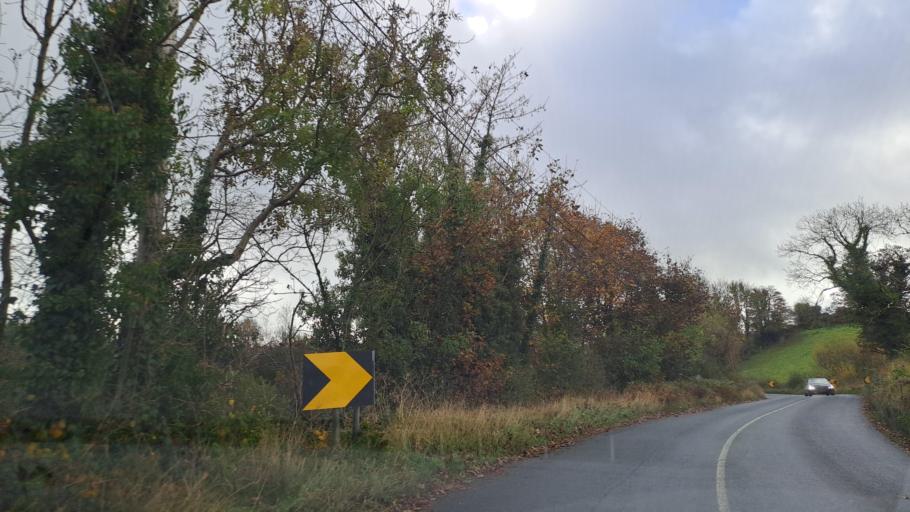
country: IE
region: Ulster
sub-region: An Cabhan
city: Virginia
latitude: 53.8572
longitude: -7.0461
